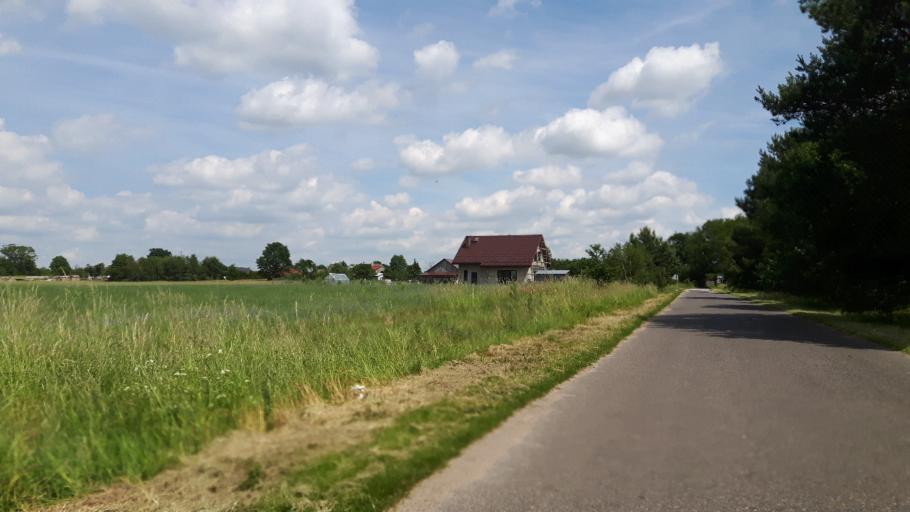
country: PL
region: West Pomeranian Voivodeship
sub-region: Powiat goleniowski
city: Osina
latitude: 53.6543
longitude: 14.9710
